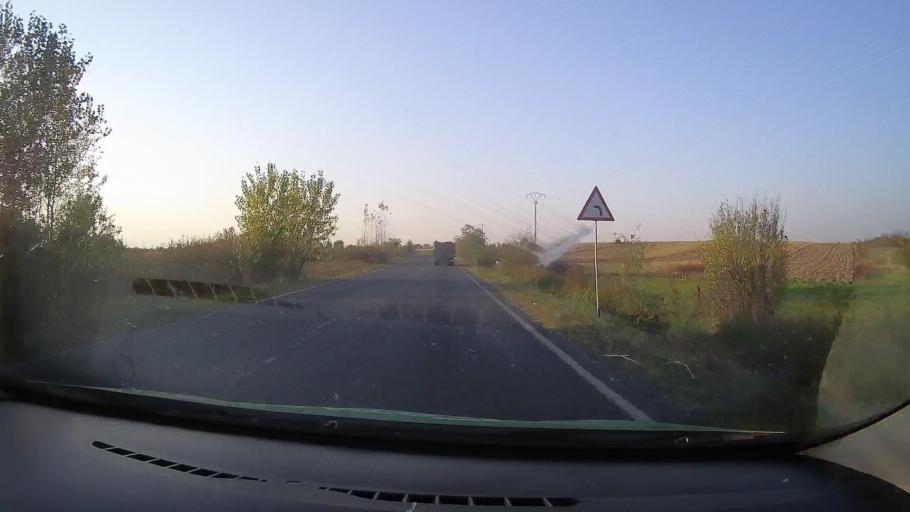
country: RO
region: Arad
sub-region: Comuna Barsa
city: Barsa
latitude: 46.3890
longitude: 22.0631
